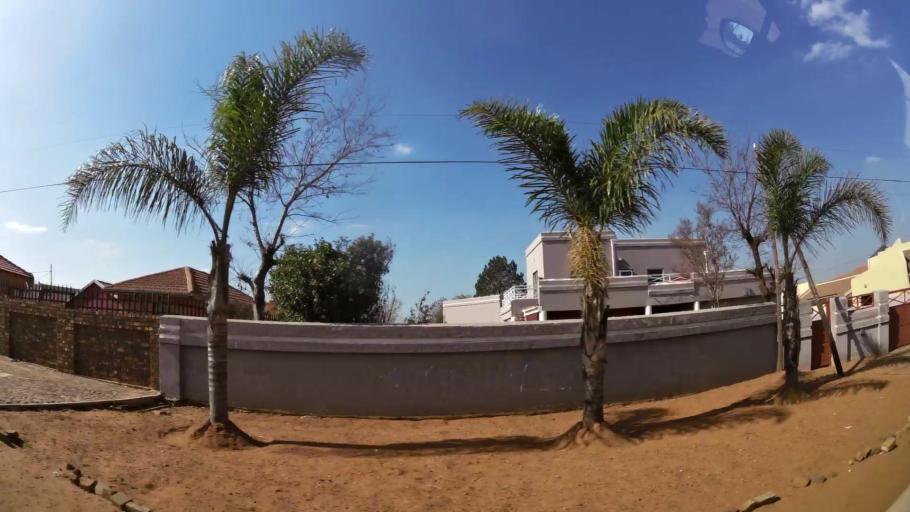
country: ZA
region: Gauteng
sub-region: City of Johannesburg Metropolitan Municipality
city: Roodepoort
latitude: -26.1683
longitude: 27.8034
